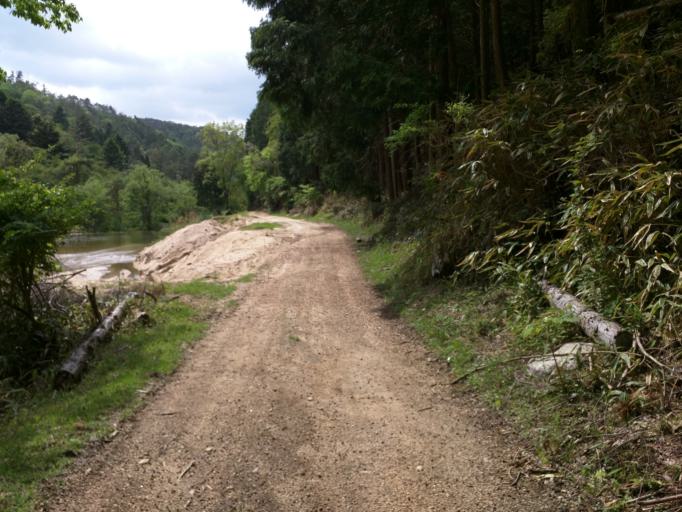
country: JP
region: Mie
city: Ueno-ebisumachi
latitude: 34.8244
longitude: 136.0008
